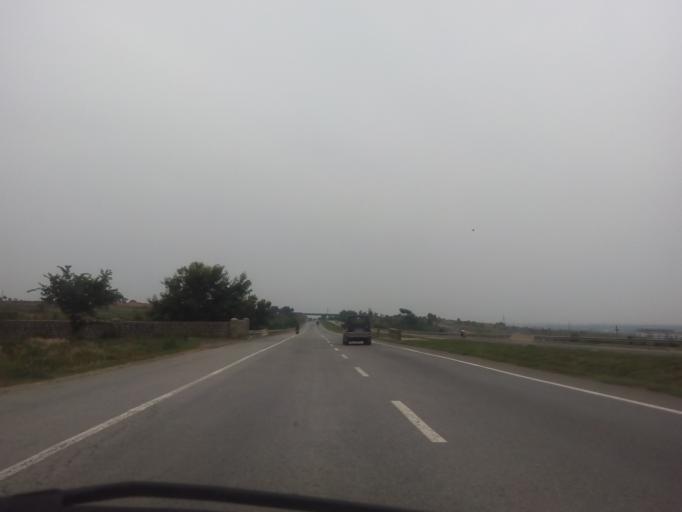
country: IN
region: Karnataka
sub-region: Bangalore Urban
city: Bangalore
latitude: 12.9201
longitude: 77.4690
